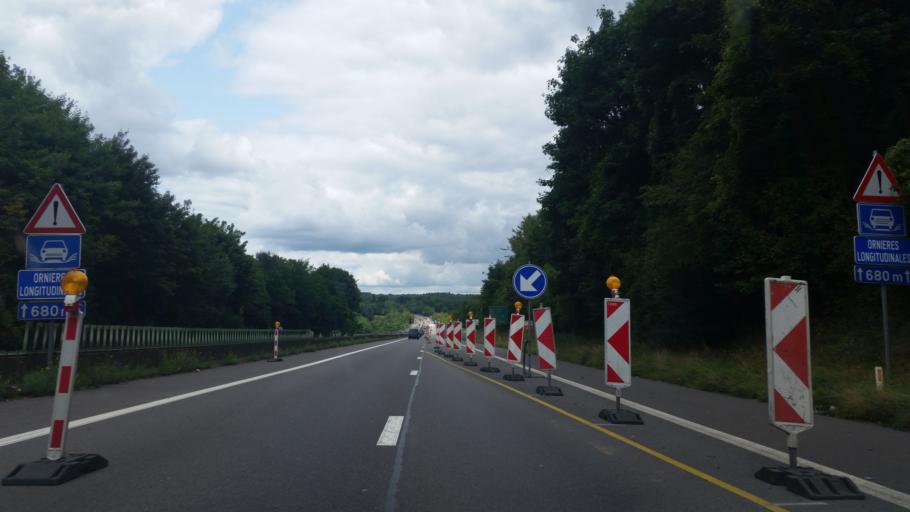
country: BE
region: Wallonia
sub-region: Province de Namur
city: Houyet
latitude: 50.2023
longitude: 5.0658
